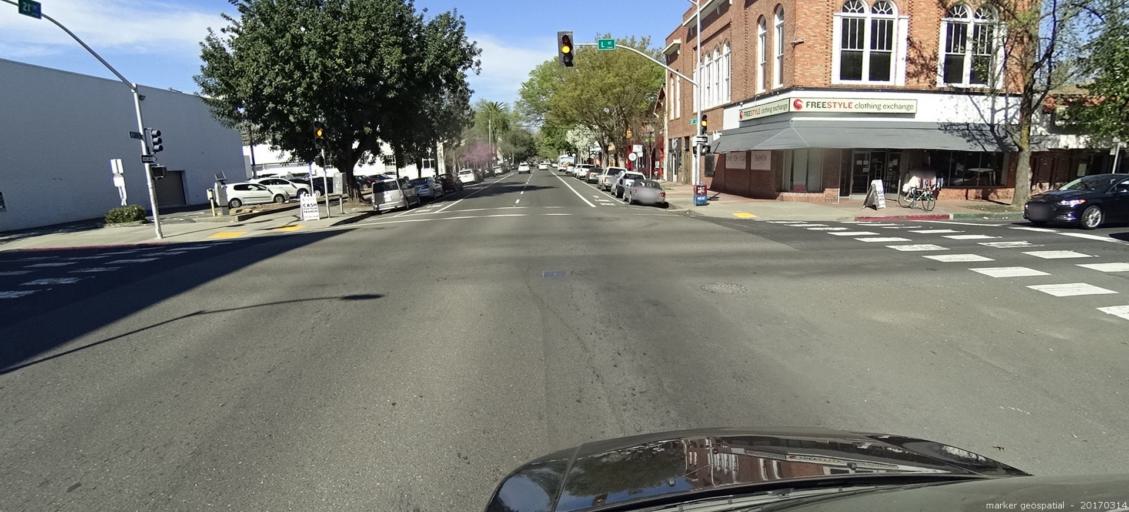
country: US
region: California
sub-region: Sacramento County
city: Sacramento
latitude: 38.5739
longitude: -121.4796
